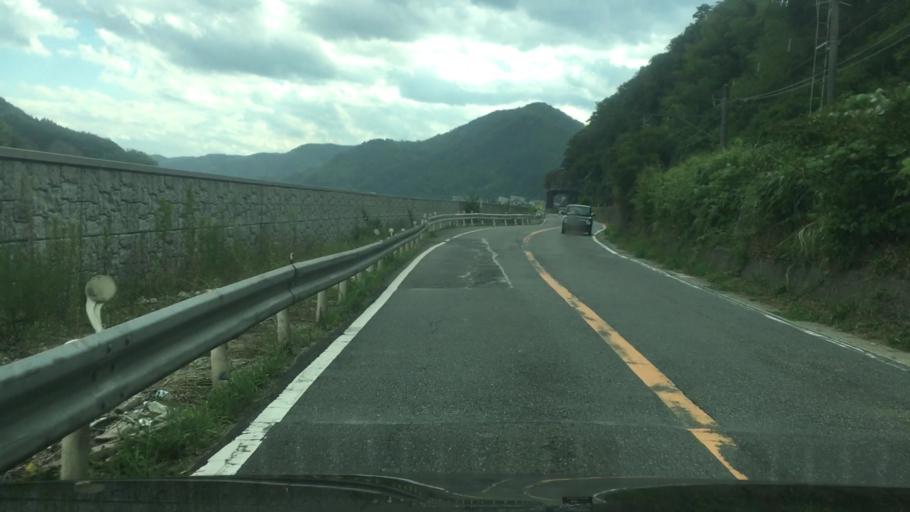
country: JP
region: Hyogo
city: Toyooka
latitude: 35.6137
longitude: 134.8078
